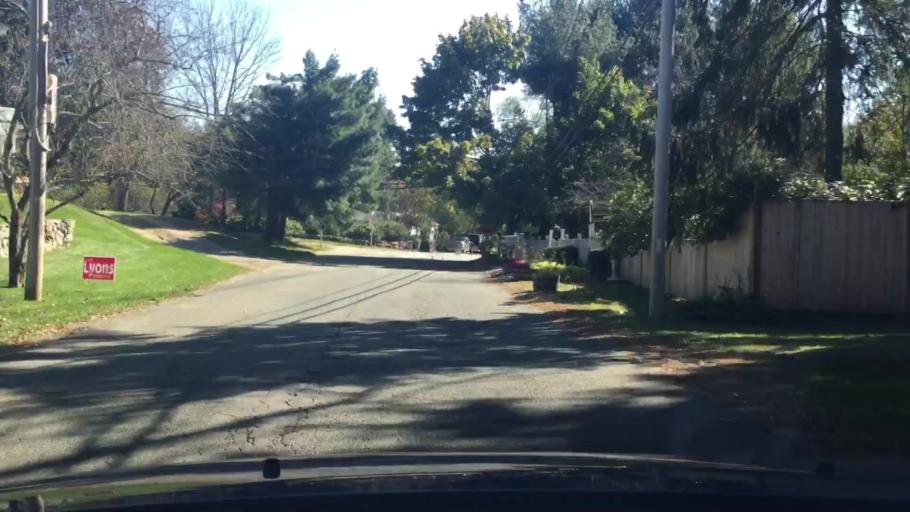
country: US
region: Massachusetts
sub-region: Essex County
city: North Andover
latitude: 42.6823
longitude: -71.0989
